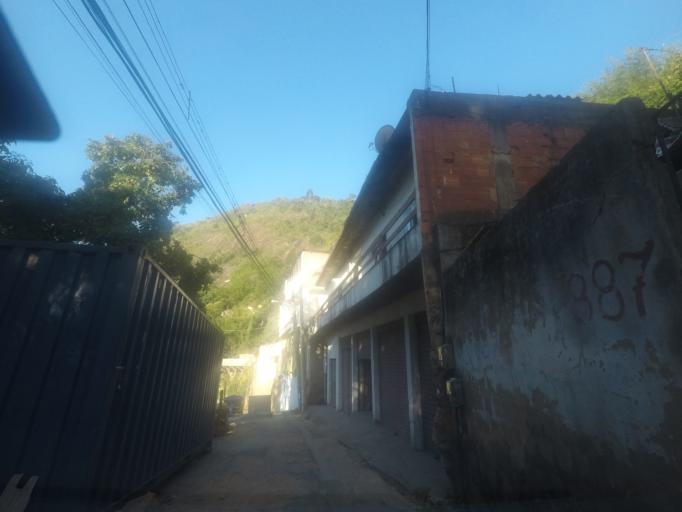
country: BR
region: Rio de Janeiro
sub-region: Petropolis
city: Petropolis
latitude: -22.4958
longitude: -43.1494
